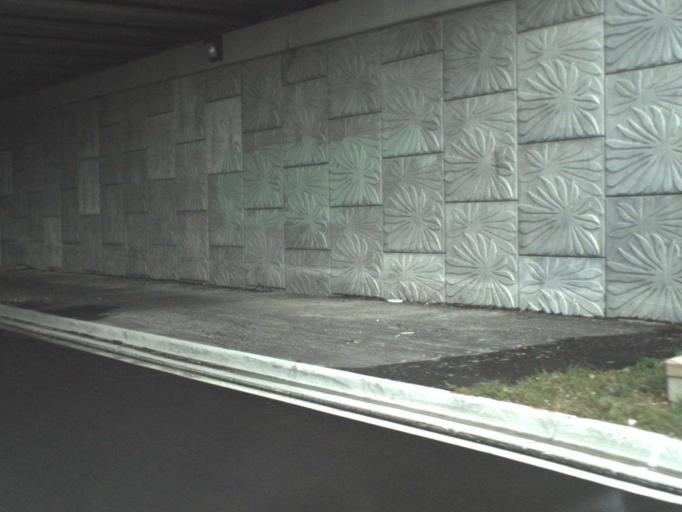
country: US
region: Florida
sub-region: Miami-Dade County
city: Flagami
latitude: 25.7700
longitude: -80.3201
